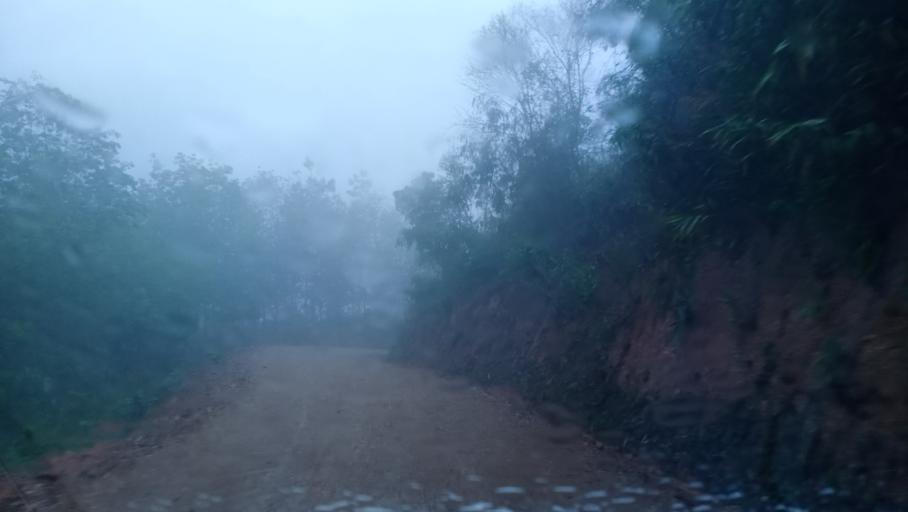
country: LA
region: Phongsali
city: Khoa
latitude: 21.1761
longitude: 102.3348
